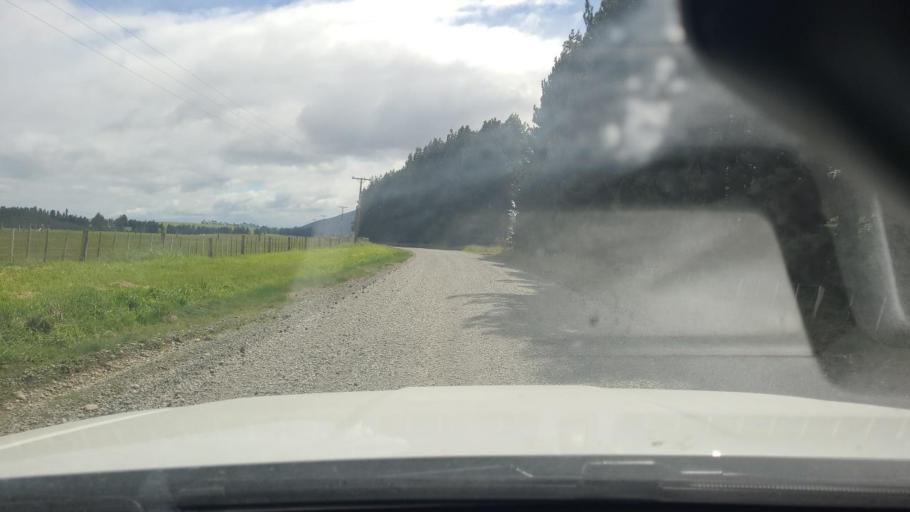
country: NZ
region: Southland
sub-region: Southland District
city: Te Anau
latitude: -45.5038
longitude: 167.8879
